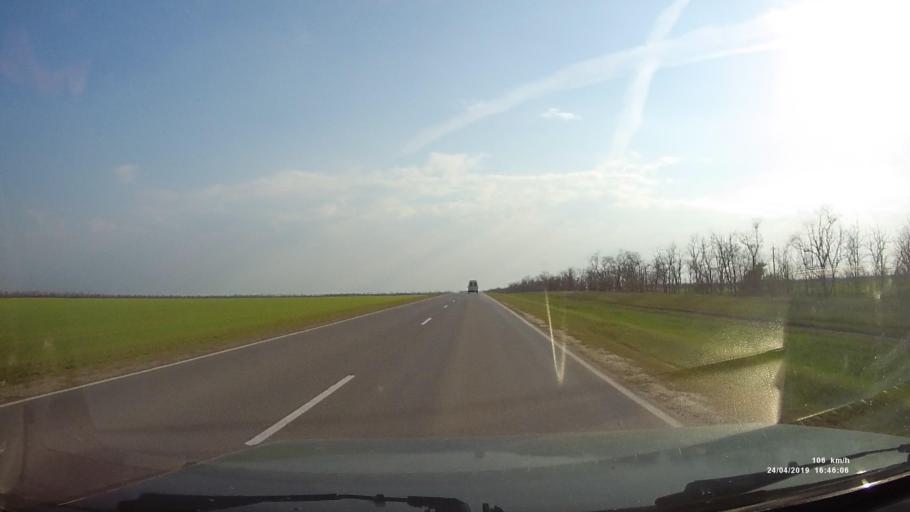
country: RU
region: Rostov
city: Gundorovskiy
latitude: 46.7613
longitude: 41.8055
